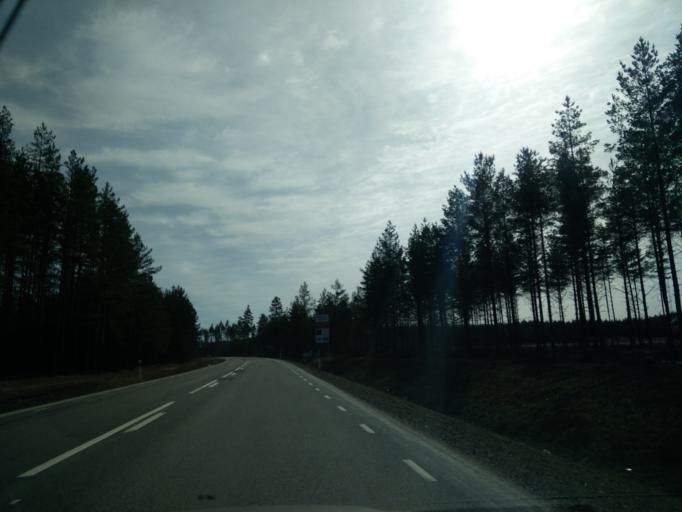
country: SE
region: Vaermland
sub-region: Hagfors Kommun
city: Hagfors
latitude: 60.0251
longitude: 13.5898
